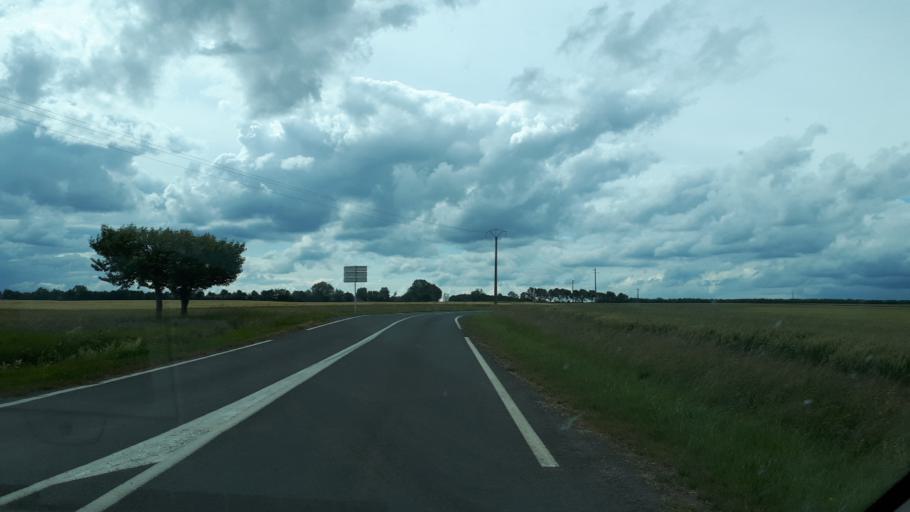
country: FR
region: Centre
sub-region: Departement du Cher
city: Gracay
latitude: 47.1223
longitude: 1.9212
